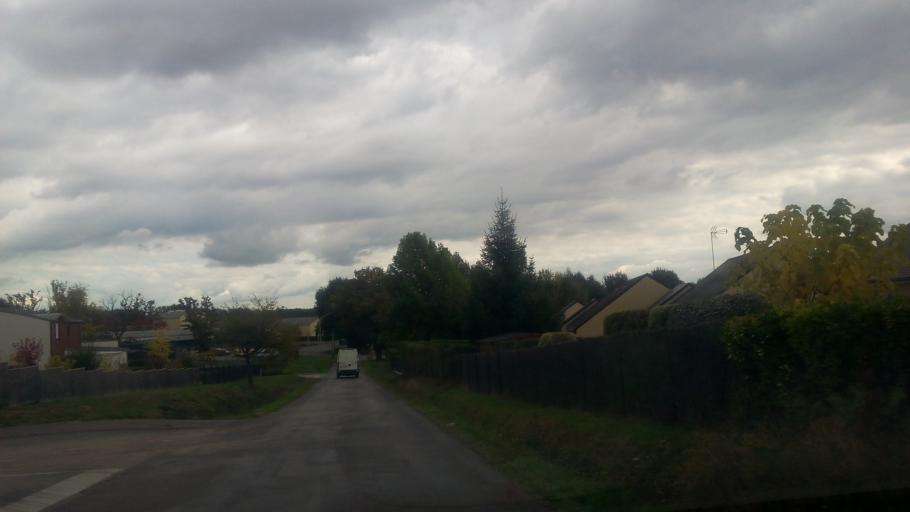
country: FR
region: Brittany
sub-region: Departement d'Ille-et-Vilaine
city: Redon
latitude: 47.6650
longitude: -2.0795
